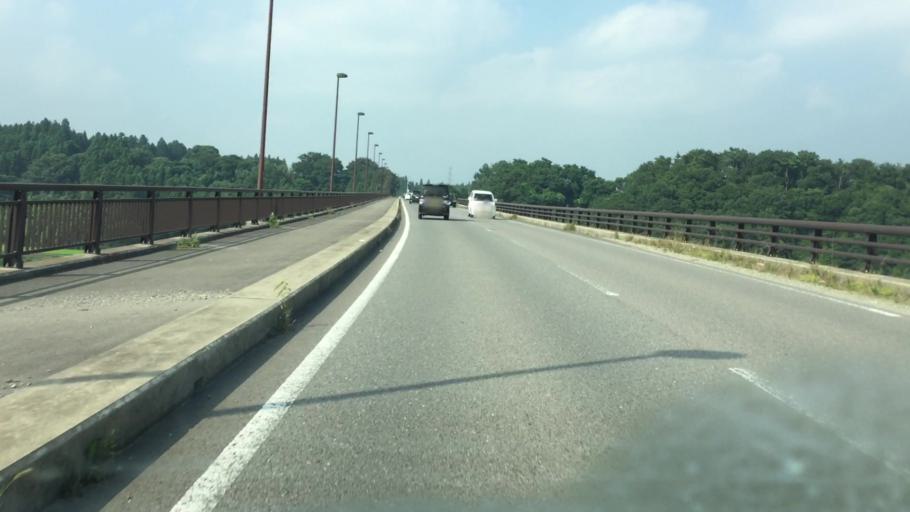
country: JP
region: Tochigi
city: Kuroiso
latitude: 37.0203
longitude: 140.0131
